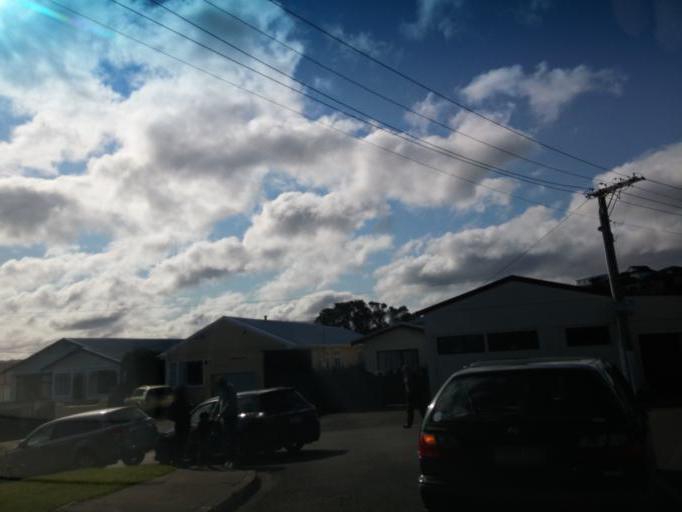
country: NZ
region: Wellington
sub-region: Wellington City
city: Wellington
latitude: -41.3175
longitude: 174.8226
